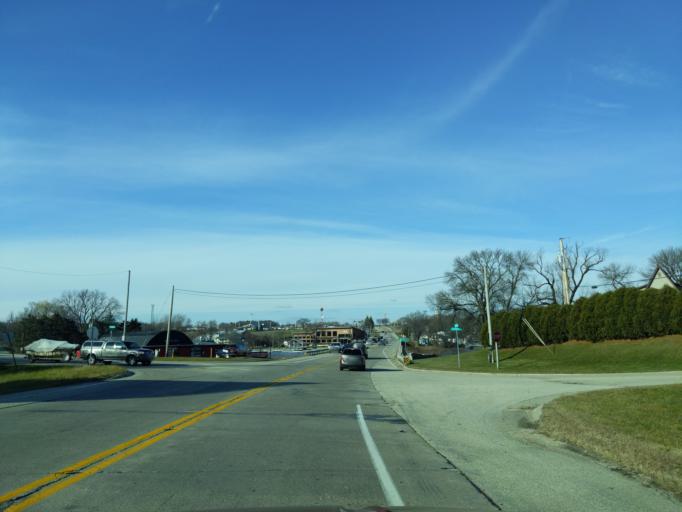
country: US
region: Wisconsin
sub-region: Rock County
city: Edgerton
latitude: 42.8283
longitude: -89.0197
